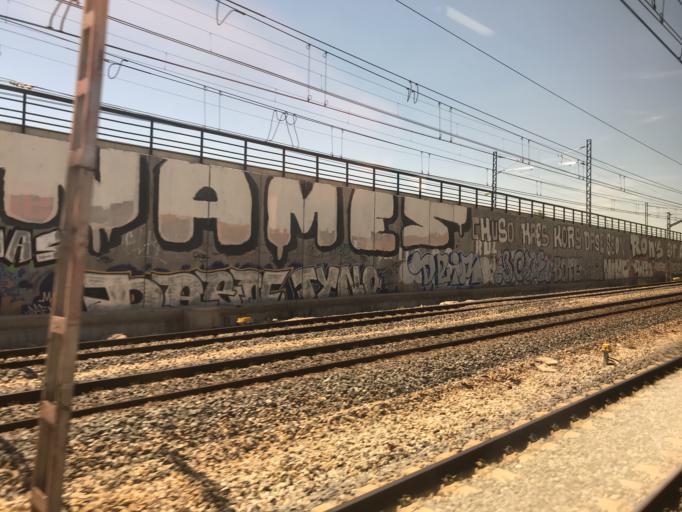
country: ES
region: Madrid
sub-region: Provincia de Madrid
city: Usera
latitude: 40.3714
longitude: -3.6788
